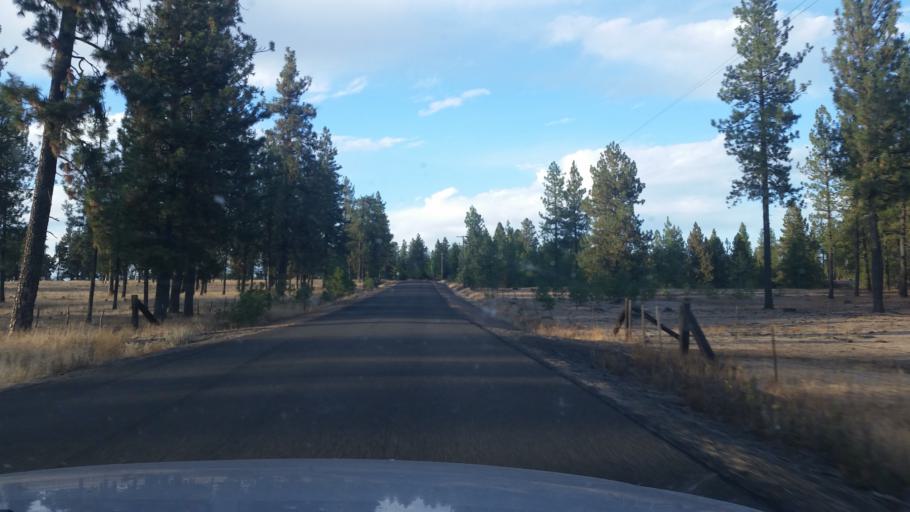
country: US
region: Washington
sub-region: Spokane County
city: Medical Lake
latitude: 47.4473
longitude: -117.7898
